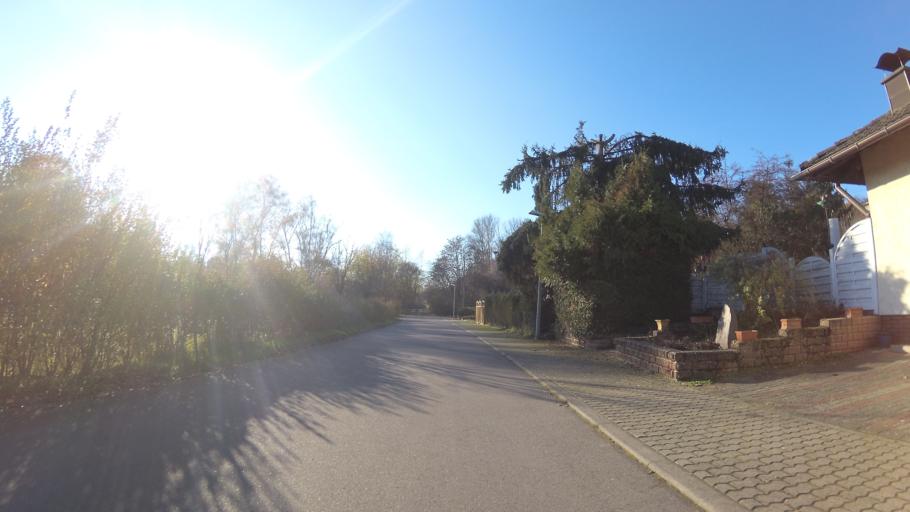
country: DE
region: Saarland
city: Bous
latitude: 49.2953
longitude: 6.8007
